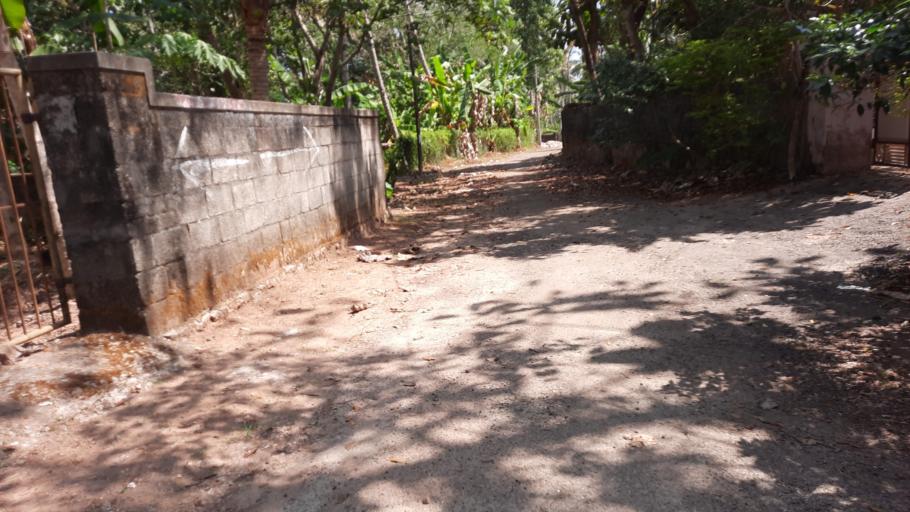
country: IN
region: Kerala
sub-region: Thiruvananthapuram
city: Thiruvananthapuram
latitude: 8.5564
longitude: 76.9314
